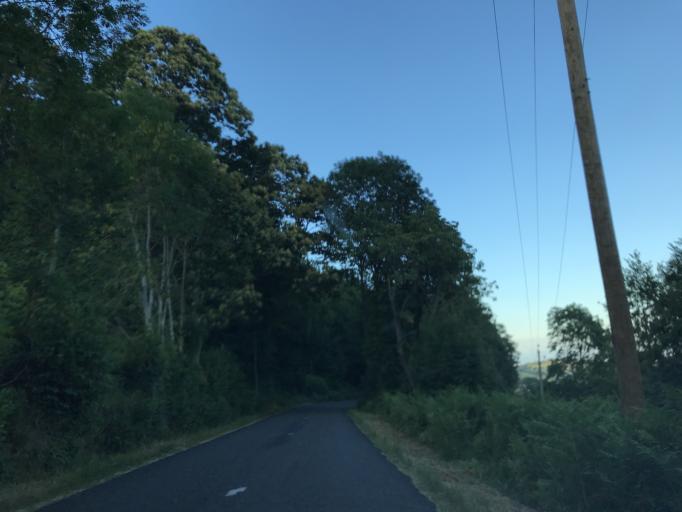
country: FR
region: Rhone-Alpes
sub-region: Departement de la Loire
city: Sail-sous-Couzan
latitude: 45.7346
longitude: 3.8621
